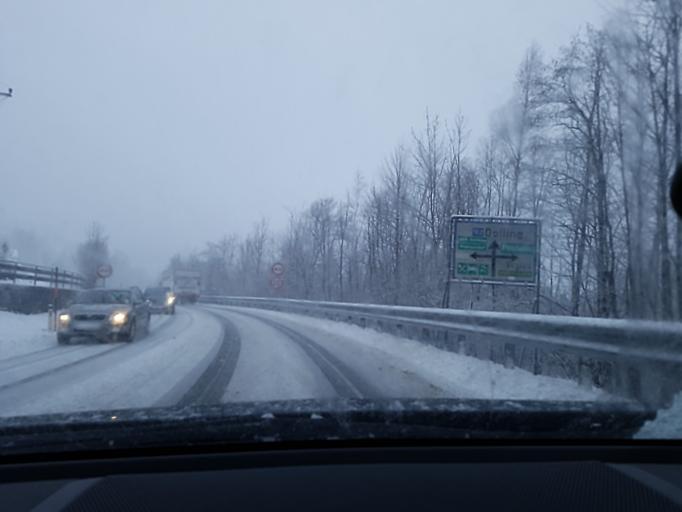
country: AT
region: Salzburg
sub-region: Politischer Bezirk Hallein
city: Abtenau
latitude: 47.5928
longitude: 13.3142
